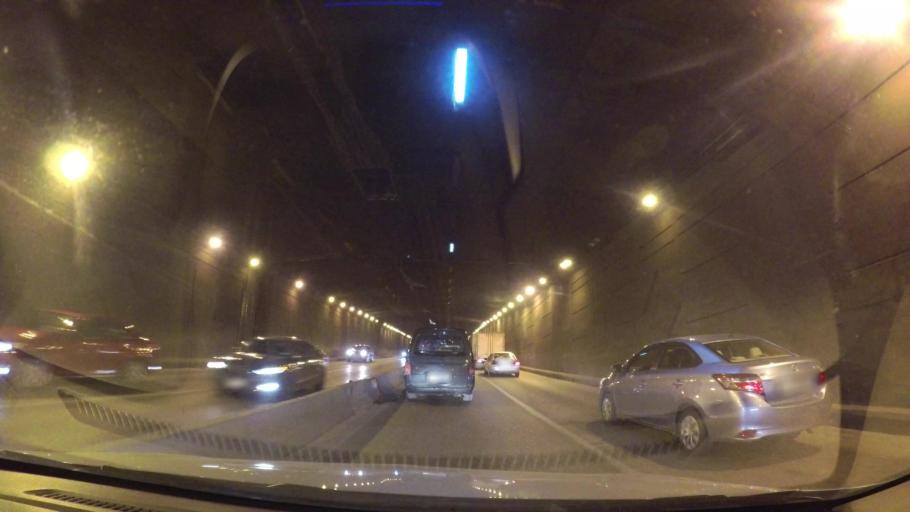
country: JO
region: Amman
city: Al Bunayyat ash Shamaliyah
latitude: 31.9461
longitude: 35.8906
